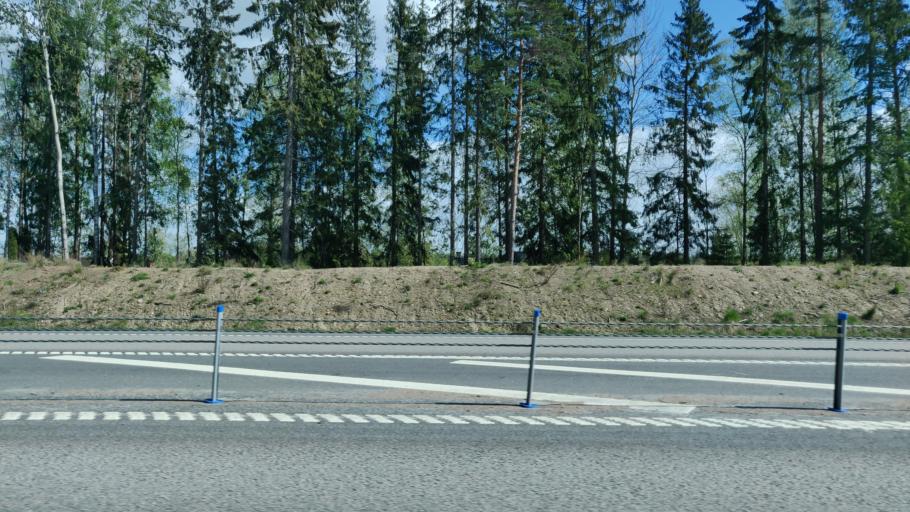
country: SE
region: Vaermland
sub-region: Karlstads Kommun
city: Karlstad
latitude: 59.4033
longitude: 13.5319
